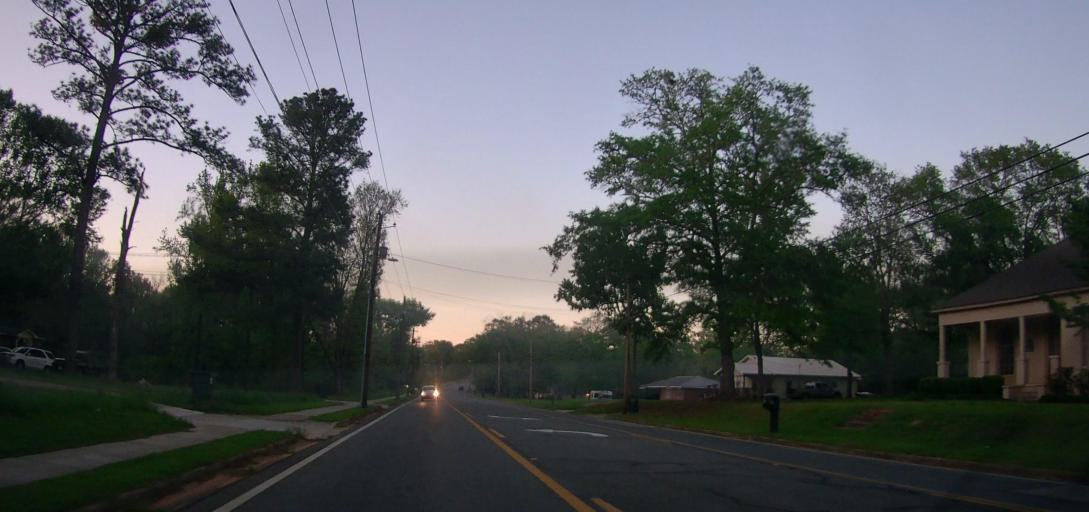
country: US
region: Georgia
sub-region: Marion County
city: Buena Vista
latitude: 32.3116
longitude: -84.5206
